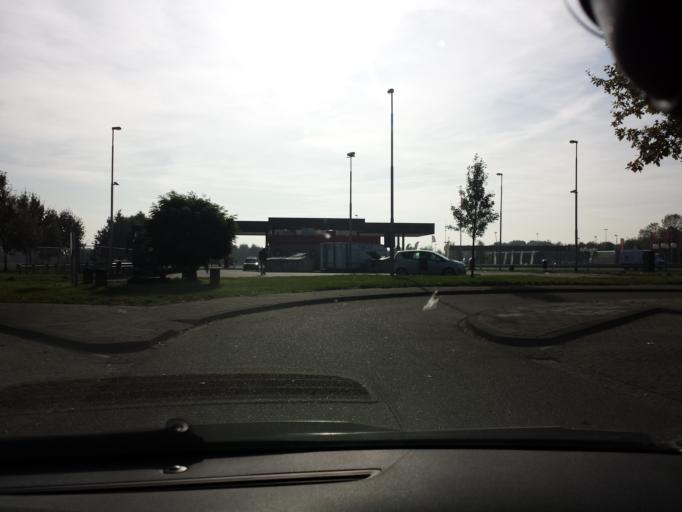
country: NL
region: Limburg
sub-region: Gemeente Venray
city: Venray
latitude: 51.5065
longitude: 6.0220
